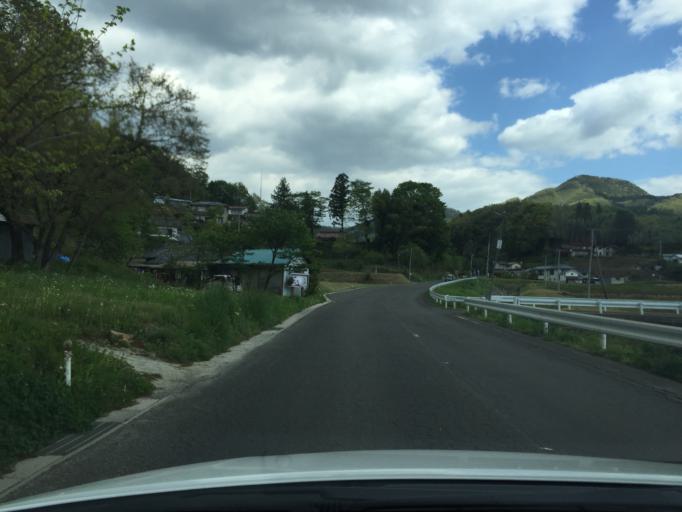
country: JP
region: Fukushima
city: Fukushima-shi
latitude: 37.6920
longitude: 140.5579
